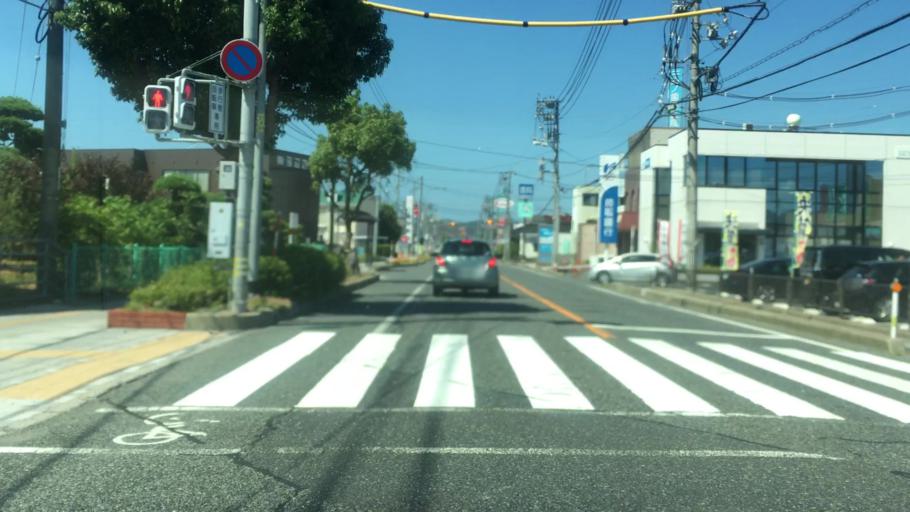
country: JP
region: Tottori
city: Tottori
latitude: 35.4796
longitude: 134.2184
